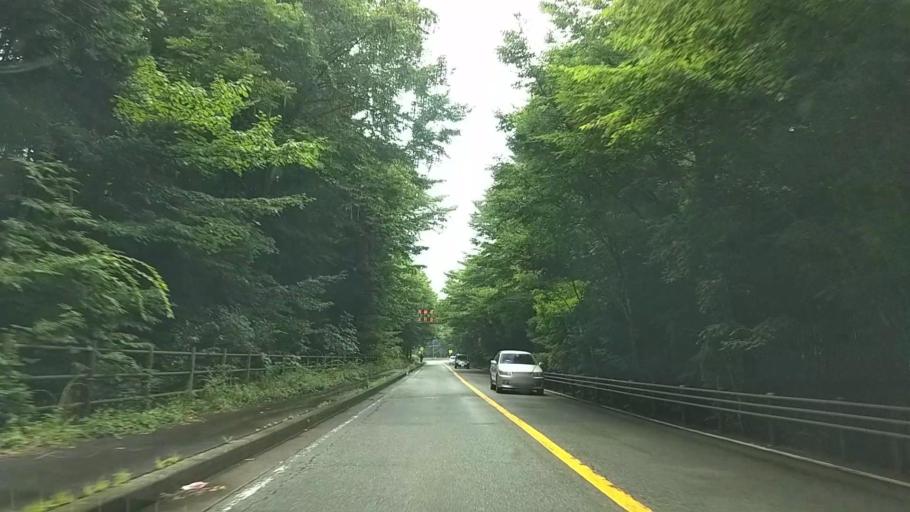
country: JP
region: Yamanashi
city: Fujikawaguchiko
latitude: 35.4663
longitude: 138.6080
